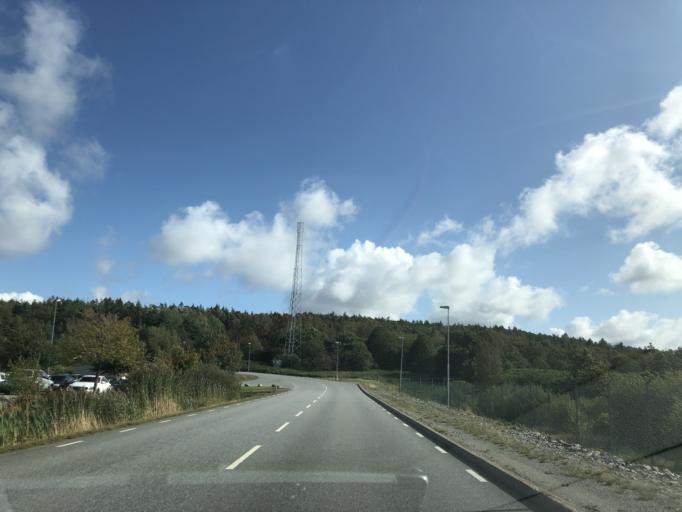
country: SE
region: Vaestra Goetaland
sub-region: Goteborg
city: Torslanda
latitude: 57.7312
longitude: 11.8450
